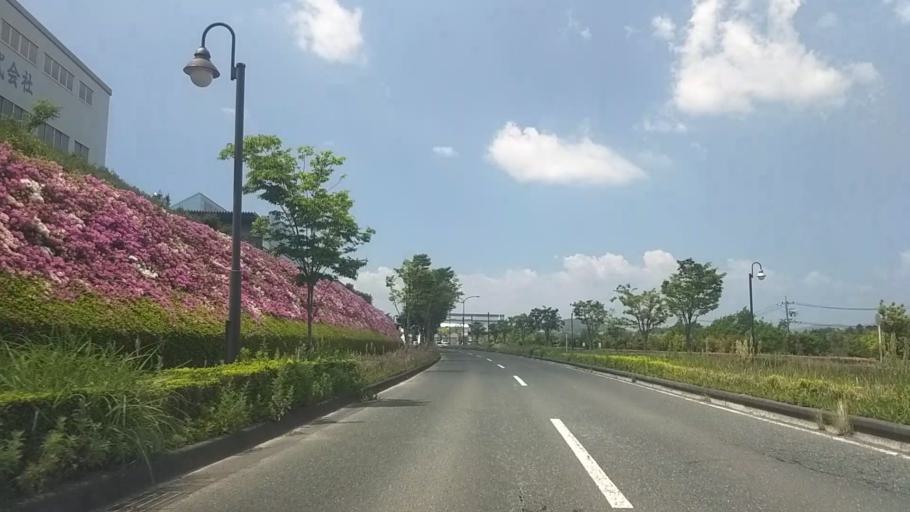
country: JP
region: Shizuoka
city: Hamamatsu
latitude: 34.7709
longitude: 137.6831
